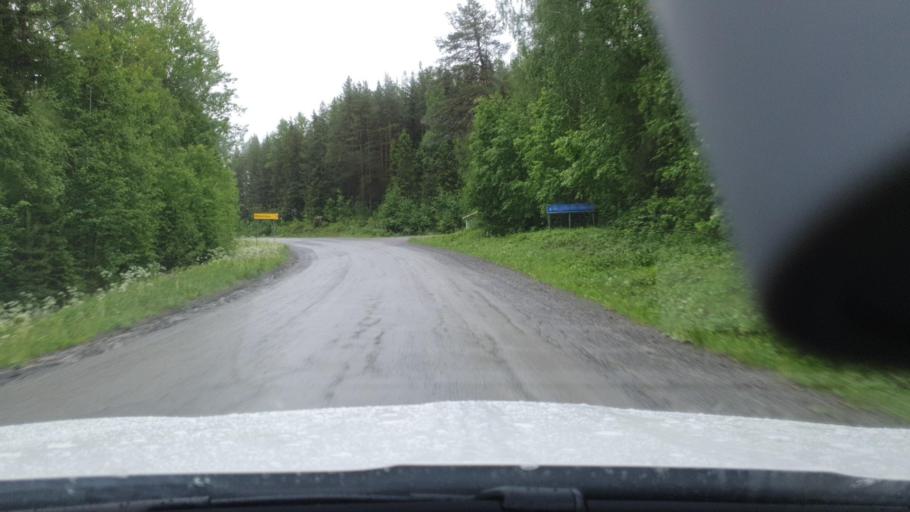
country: SE
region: Vaesterbotten
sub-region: Skelleftea Kommun
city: Burtraesk
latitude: 64.3617
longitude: 20.4120
